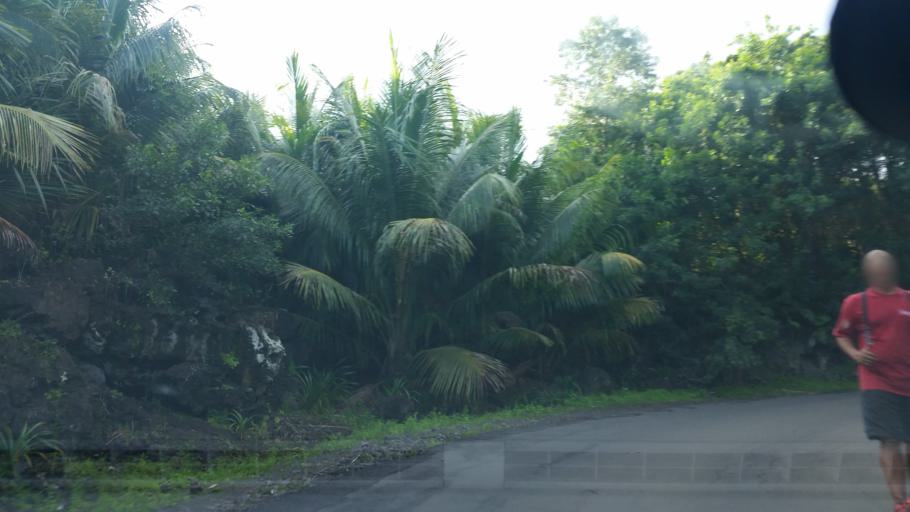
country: RE
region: Reunion
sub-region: Reunion
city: Saint-Joseph
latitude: -21.3784
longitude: 55.6705
